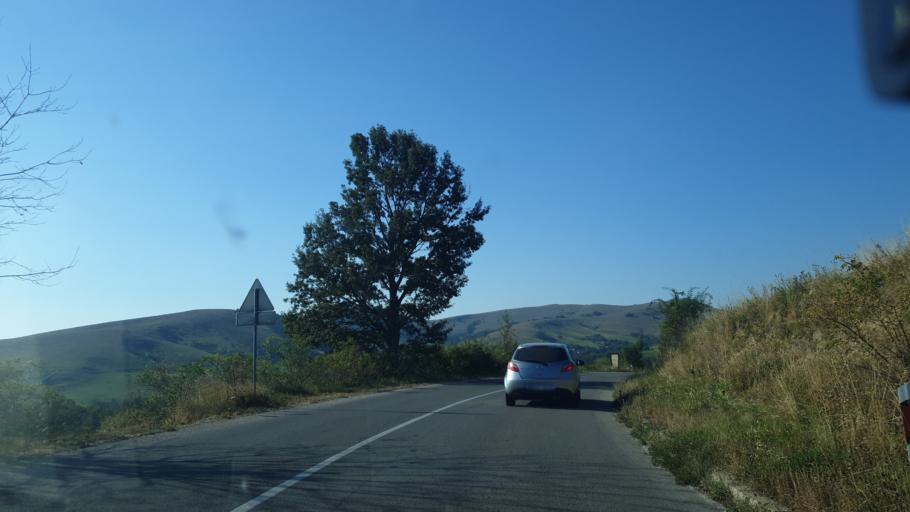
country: RS
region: Central Serbia
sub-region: Zlatiborski Okrug
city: Cajetina
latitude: 43.7155
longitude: 19.7625
